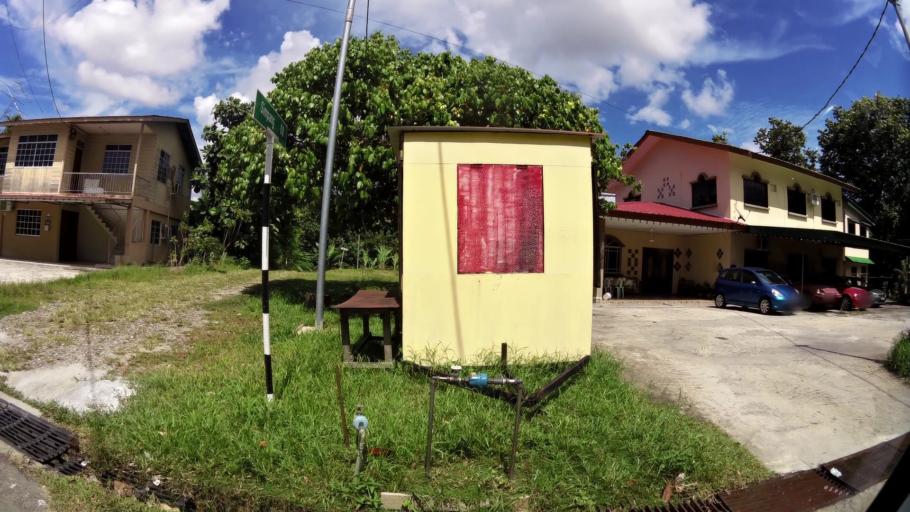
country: BN
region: Brunei and Muara
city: Bandar Seri Begawan
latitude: 4.9712
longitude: 114.9411
